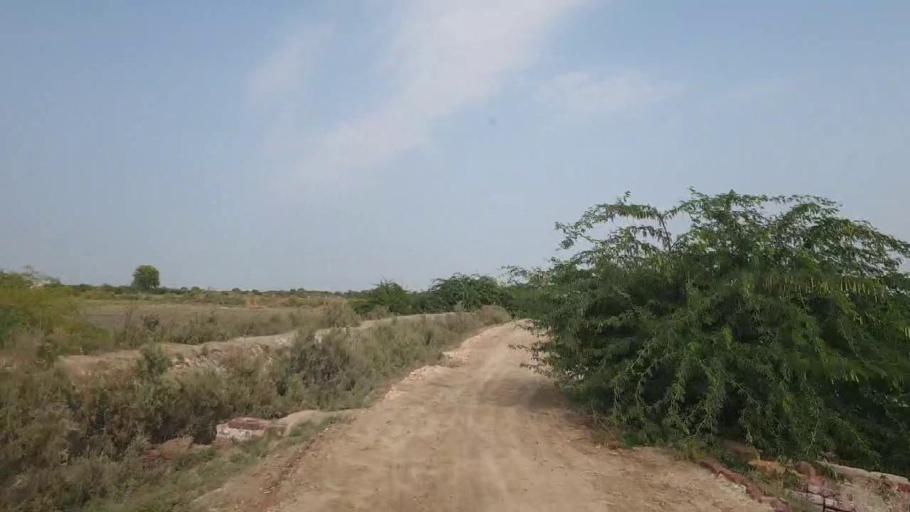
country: PK
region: Sindh
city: Kadhan
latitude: 24.4431
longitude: 68.8004
